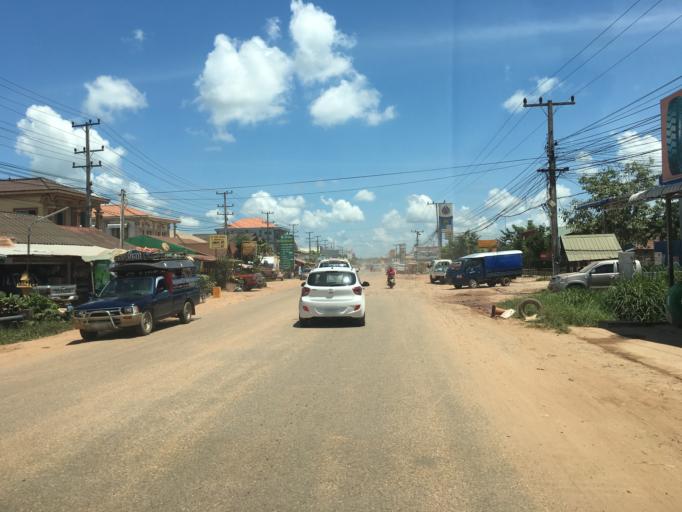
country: TH
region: Nong Khai
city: Si Chiang Mai
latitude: 18.0202
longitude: 102.5468
